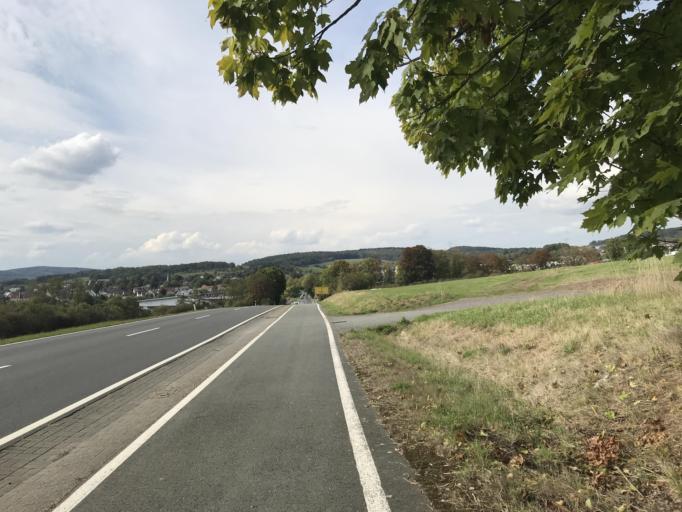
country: DE
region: Hesse
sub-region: Regierungsbezirk Giessen
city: Asslar
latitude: 50.5972
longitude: 8.4302
